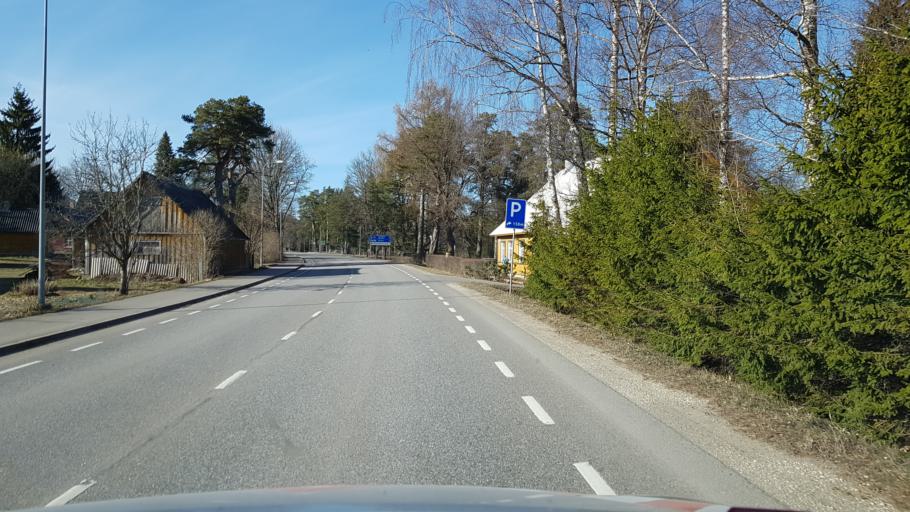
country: EE
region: Laeaene-Virumaa
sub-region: Vinni vald
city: Vinni
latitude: 59.1635
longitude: 26.5870
